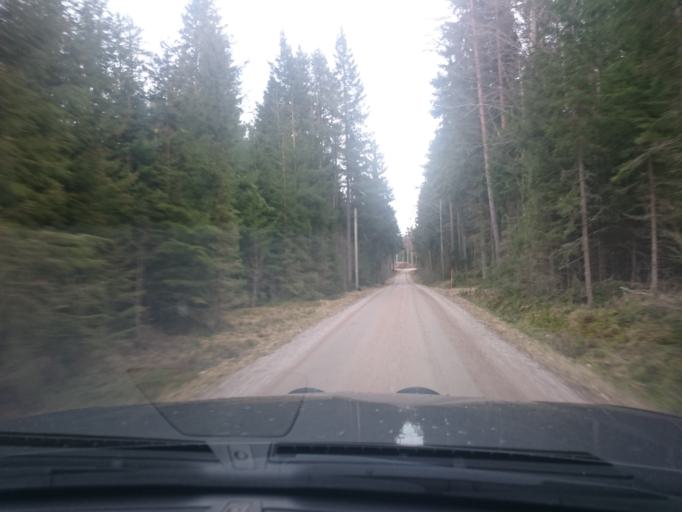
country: SE
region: Joenkoeping
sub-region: Vetlanda Kommun
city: Vetlanda
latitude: 57.2941
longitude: 15.1440
